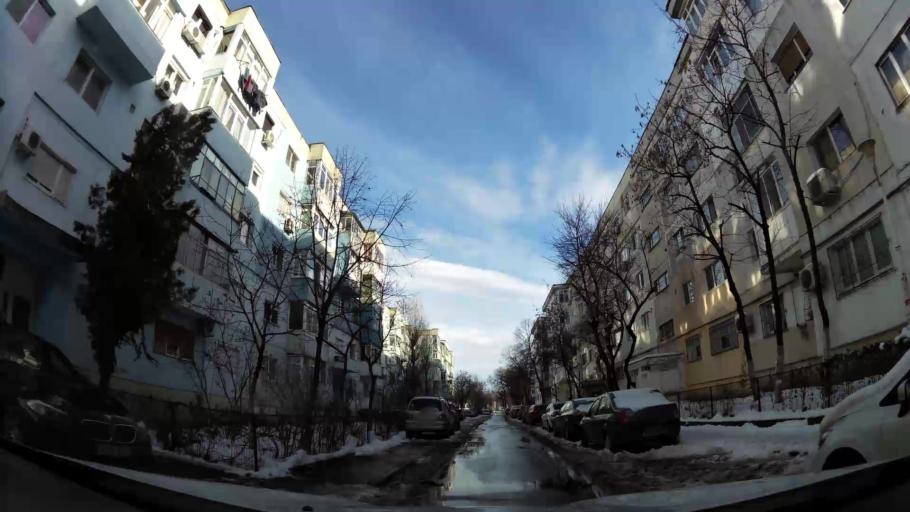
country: RO
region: Bucuresti
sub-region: Municipiul Bucuresti
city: Bucuresti
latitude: 44.3835
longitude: 26.0976
